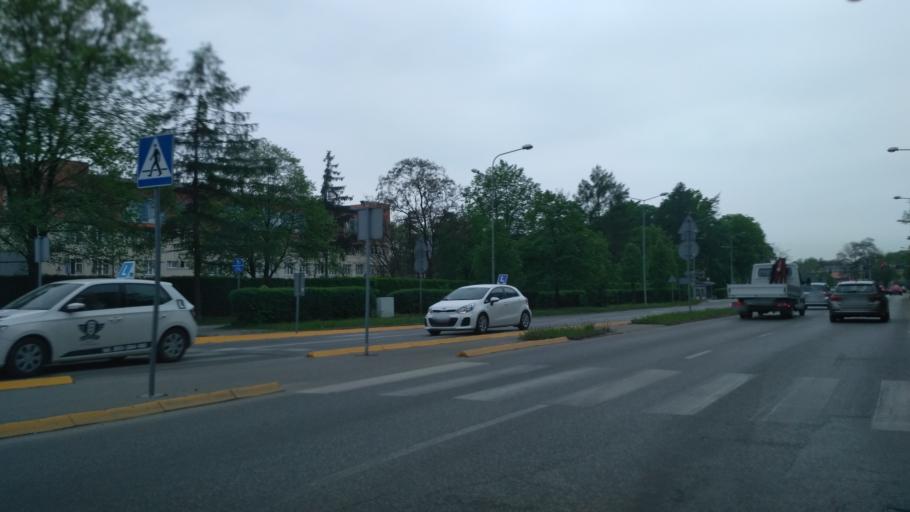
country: PL
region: Lesser Poland Voivodeship
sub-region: Powiat tarnowski
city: Tarnow
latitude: 50.0183
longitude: 20.9962
